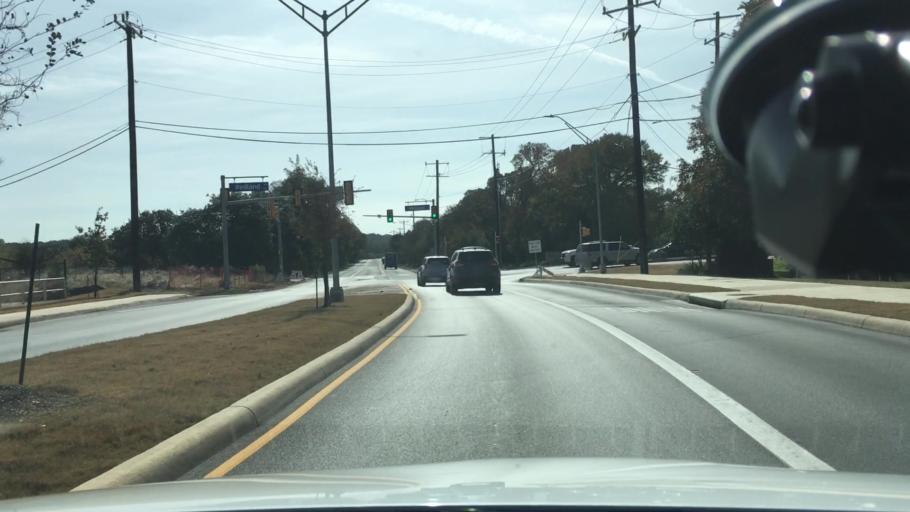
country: US
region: Texas
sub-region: Bexar County
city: Hollywood Park
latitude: 29.5937
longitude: -98.4245
